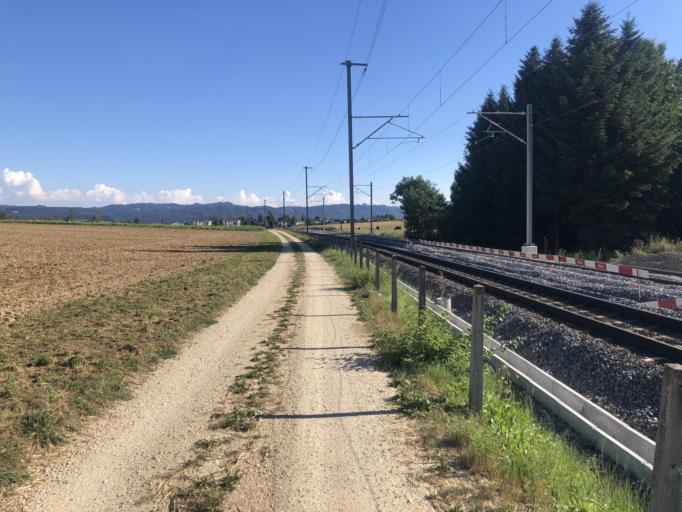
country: CH
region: Bern
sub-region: Bern-Mittelland District
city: Jegenstorf
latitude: 47.0629
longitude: 7.5069
